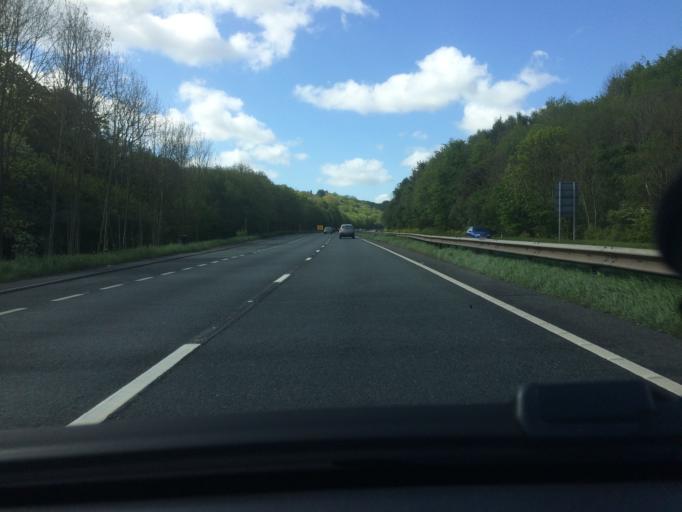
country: GB
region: Wales
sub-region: Wrexham
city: Gresford
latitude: 53.0994
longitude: -2.9634
